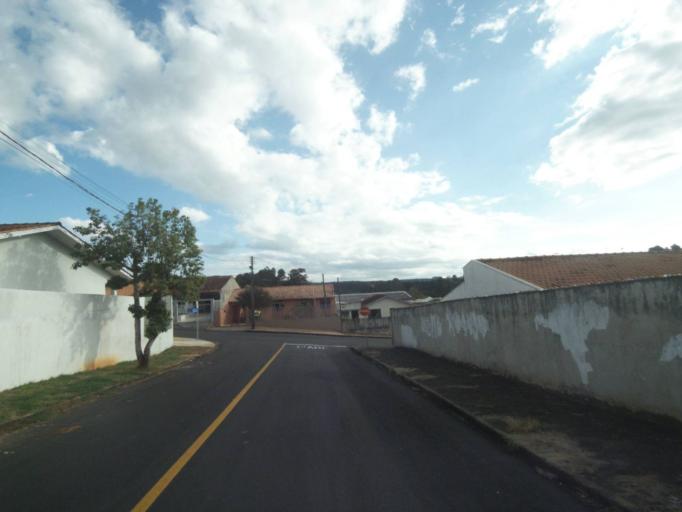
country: BR
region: Parana
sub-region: Telemaco Borba
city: Telemaco Borba
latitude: -24.3389
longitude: -50.6132
